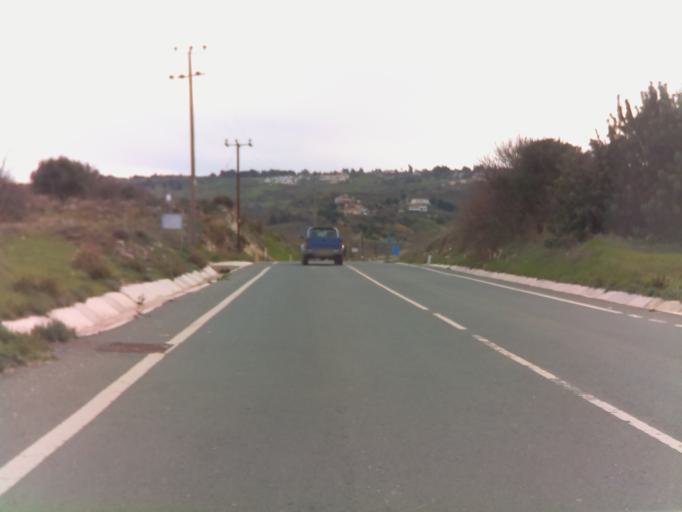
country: CY
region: Pafos
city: Polis
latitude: 34.9840
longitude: 32.4061
